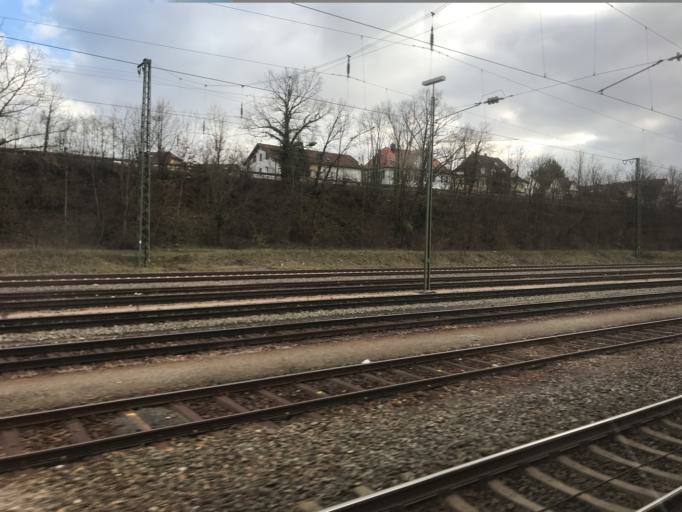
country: DE
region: Baden-Wuerttemberg
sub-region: Freiburg Region
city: Weil am Rhein
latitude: 47.5988
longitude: 7.6117
